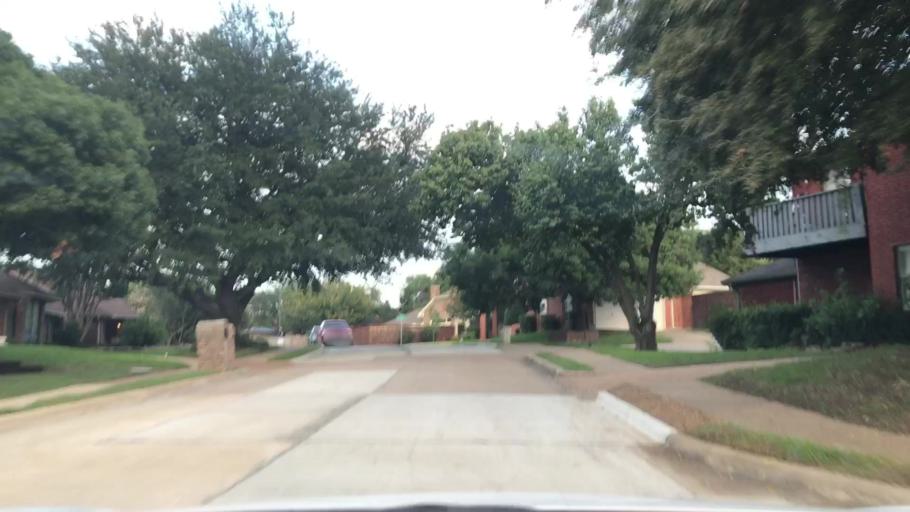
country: US
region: Texas
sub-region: Dallas County
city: Addison
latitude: 33.0054
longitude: -96.8638
